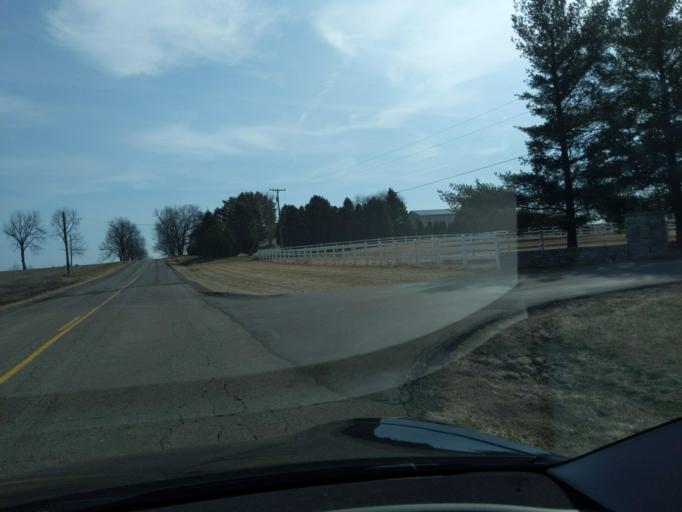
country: US
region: Michigan
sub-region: Ingham County
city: Williamston
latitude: 42.6594
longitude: -84.2436
